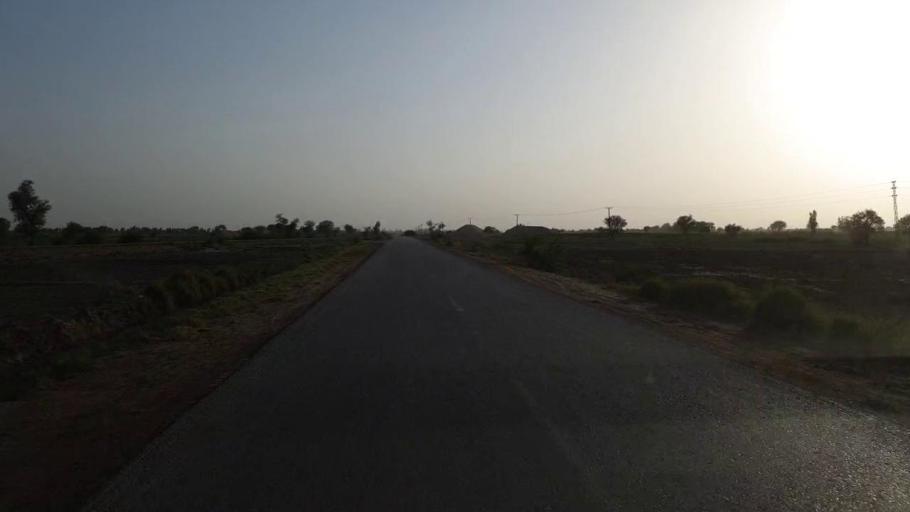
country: PK
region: Sindh
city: Jam Sahib
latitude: 26.2836
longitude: 68.5865
